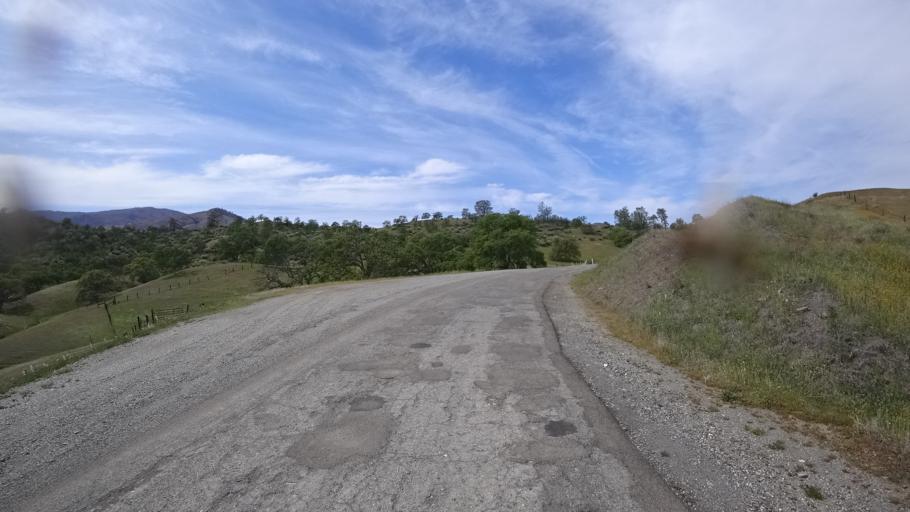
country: US
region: California
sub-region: Glenn County
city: Willows
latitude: 39.6171
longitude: -122.5913
